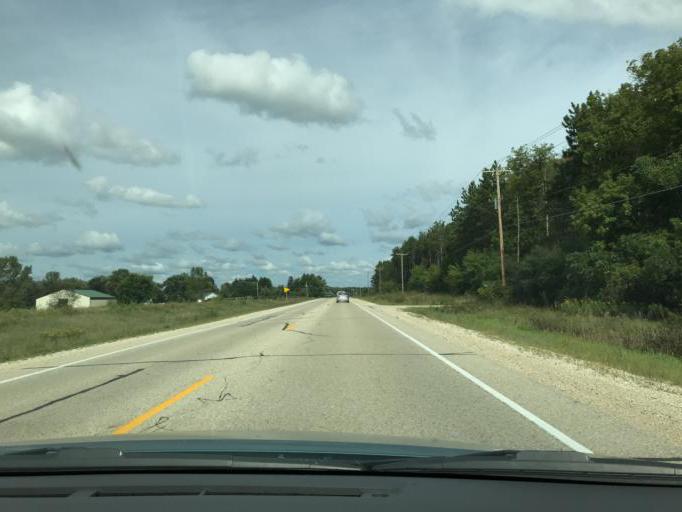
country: US
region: Wisconsin
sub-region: Racine County
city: Bohners Lake
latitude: 42.6227
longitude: -88.2401
